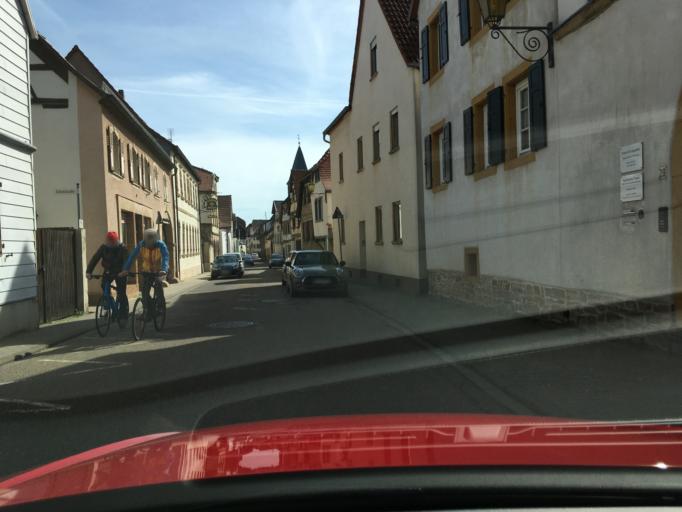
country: DE
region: Rheinland-Pfalz
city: Neustadt
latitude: 49.3708
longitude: 8.1682
